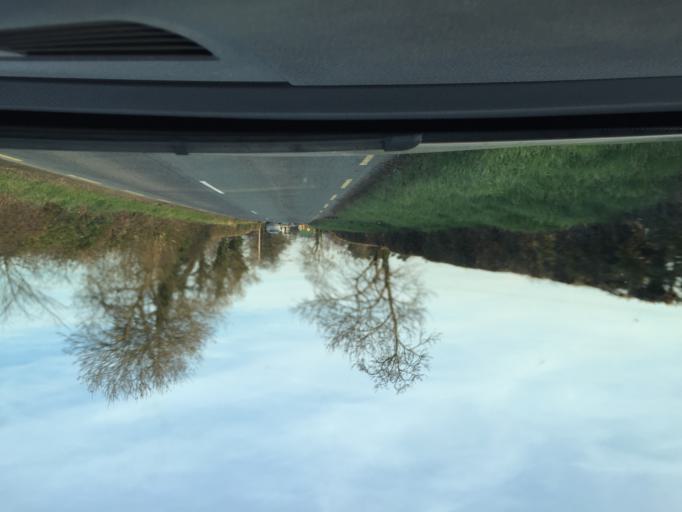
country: IE
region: Leinster
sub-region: An Mhi
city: Dunboyne
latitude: 53.3866
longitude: -6.4522
